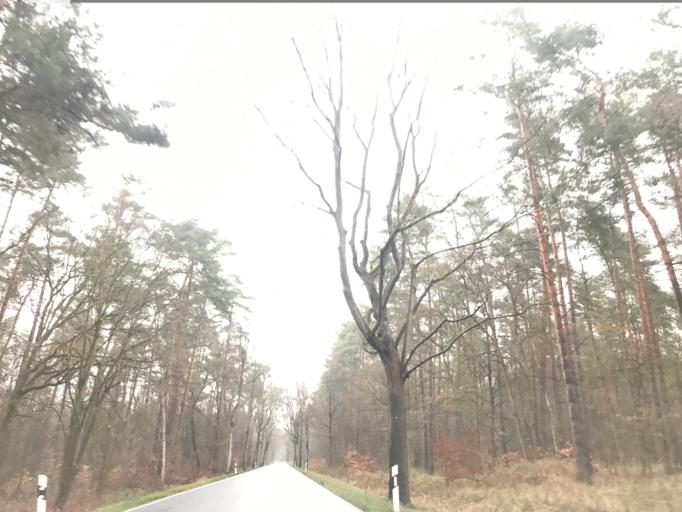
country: DE
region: Brandenburg
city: Brieselang
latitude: 52.6199
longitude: 12.9721
